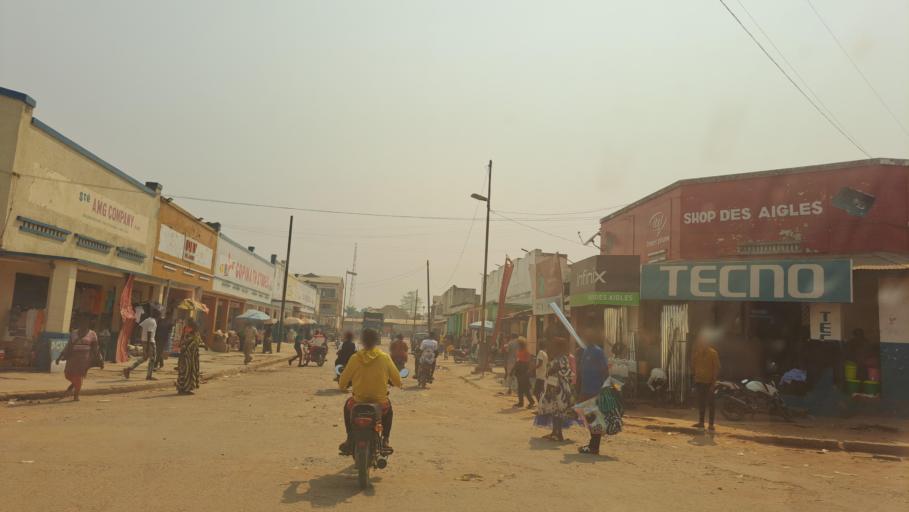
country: CD
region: Kasai-Occidental
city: Kananga
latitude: -5.8957
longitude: 22.4075
